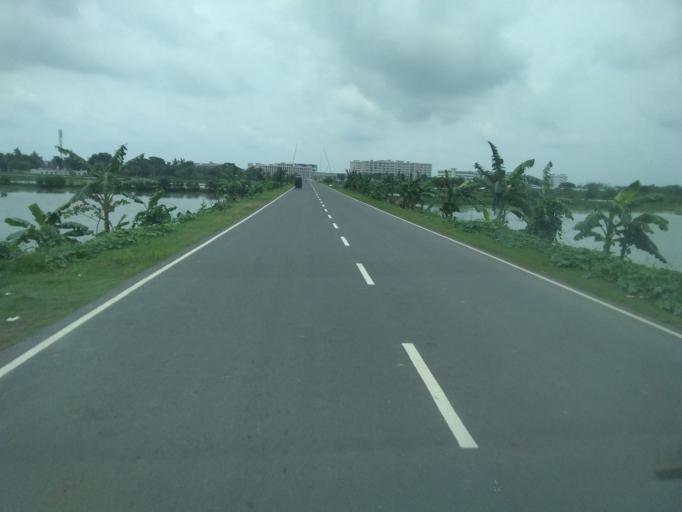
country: BD
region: Khulna
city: Satkhira
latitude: 22.6961
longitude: 89.0514
